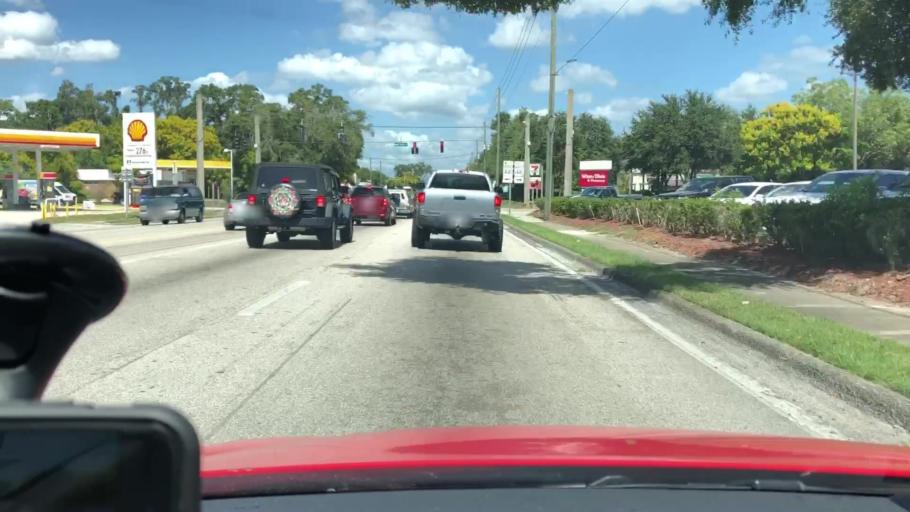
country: US
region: Florida
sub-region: Volusia County
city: West DeLand
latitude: 29.0272
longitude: -81.3241
